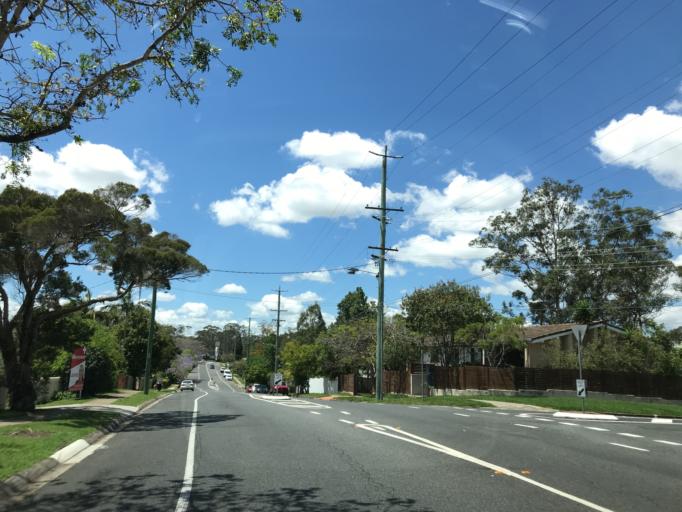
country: AU
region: Queensland
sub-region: Brisbane
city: Kenmore Hills
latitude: -27.5190
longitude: 152.9380
